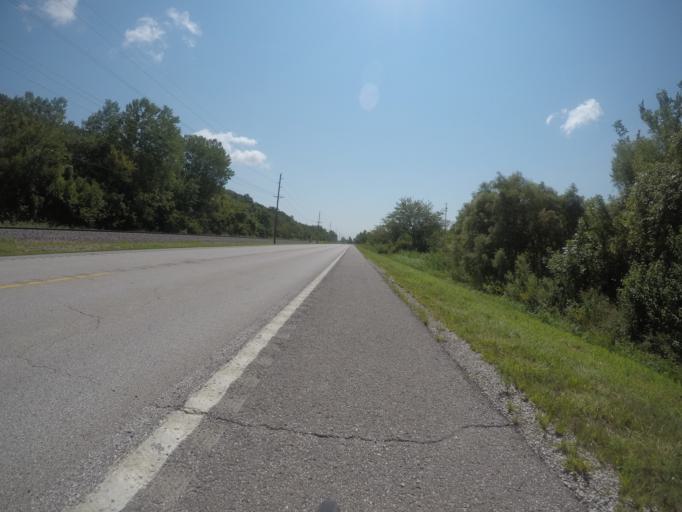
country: US
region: Missouri
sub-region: Platte County
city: Weston
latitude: 39.4631
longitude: -94.9729
